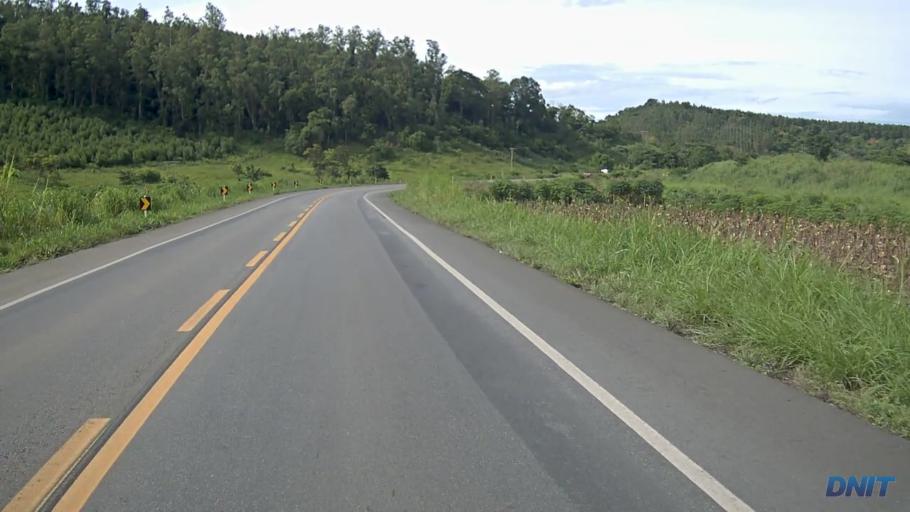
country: BR
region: Minas Gerais
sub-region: Belo Oriente
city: Belo Oriente
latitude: -19.2716
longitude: -42.3566
